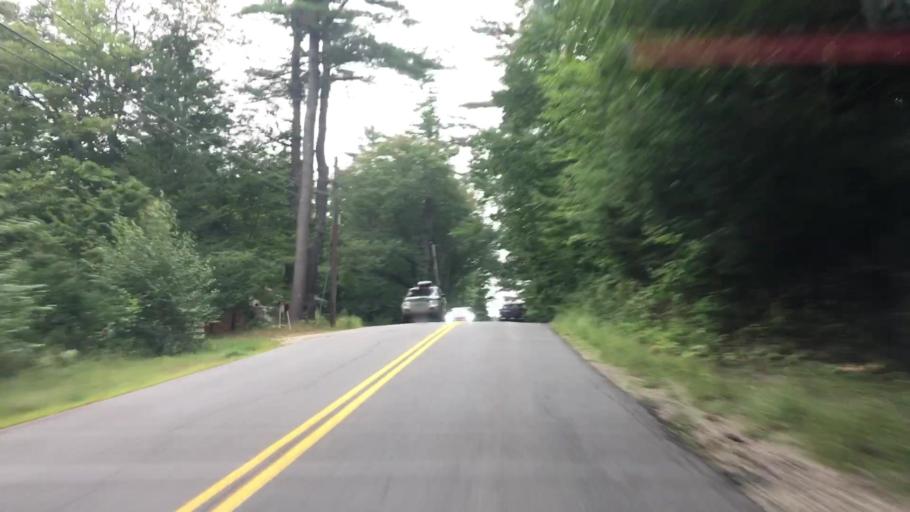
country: US
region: Maine
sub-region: Cumberland County
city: Freeport
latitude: 43.8773
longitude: -70.1537
